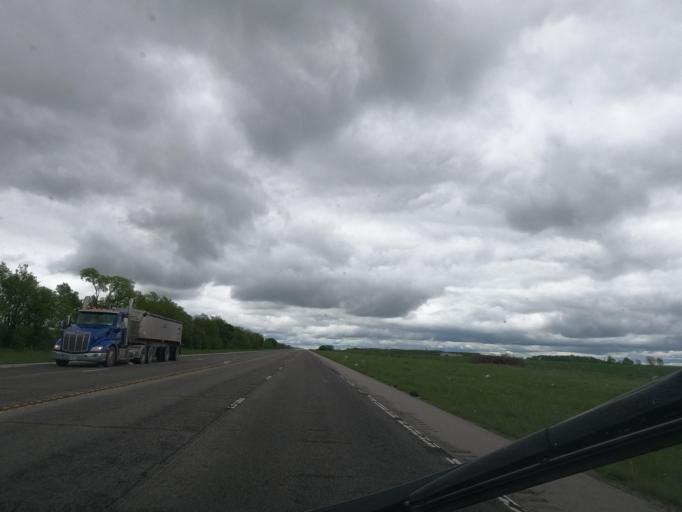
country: US
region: Kansas
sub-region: Montgomery County
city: Cherryvale
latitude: 37.3466
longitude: -95.5069
